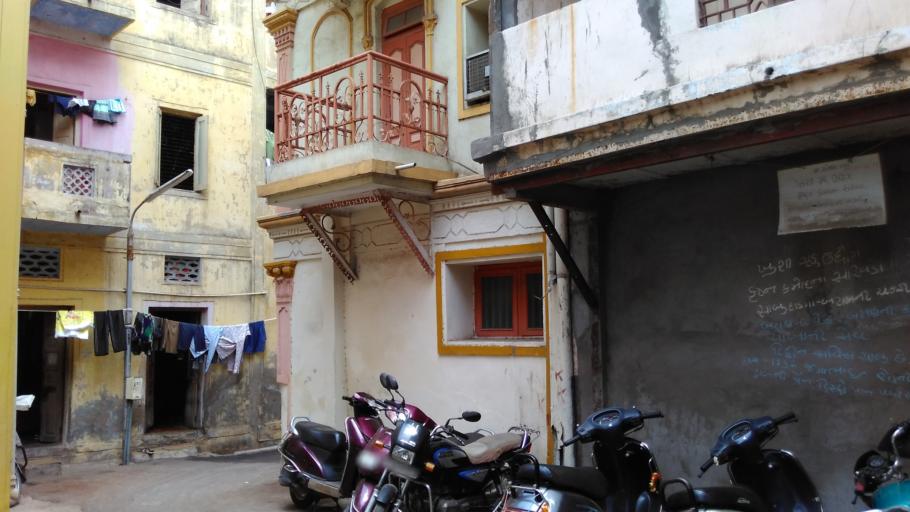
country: IN
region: Gujarat
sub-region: Ahmadabad
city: Ahmedabad
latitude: 23.0186
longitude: 72.5910
